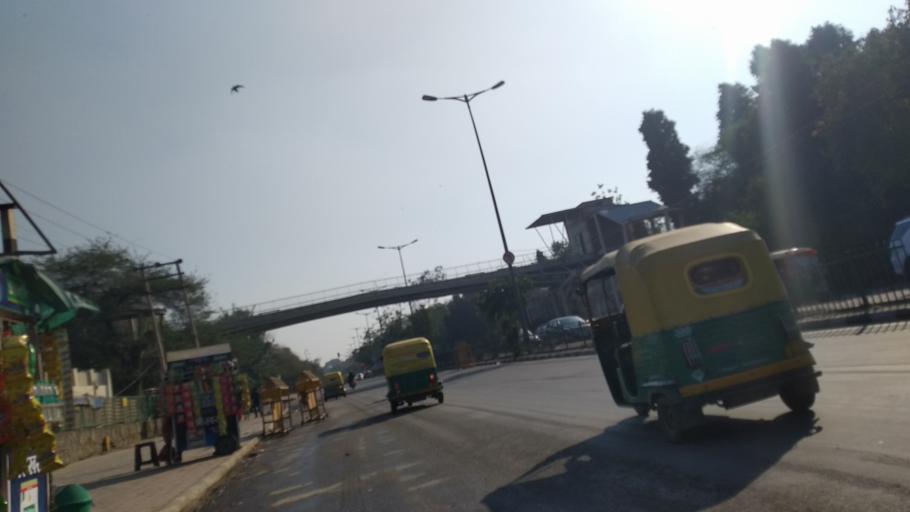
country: IN
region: NCT
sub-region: New Delhi
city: New Delhi
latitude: 28.6143
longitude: 77.2403
